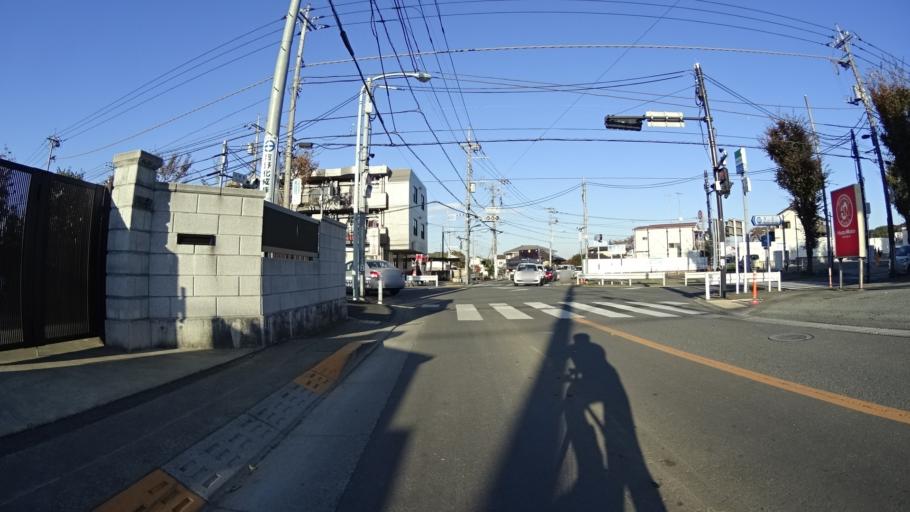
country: JP
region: Tokyo
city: Hachioji
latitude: 35.6724
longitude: 139.2592
